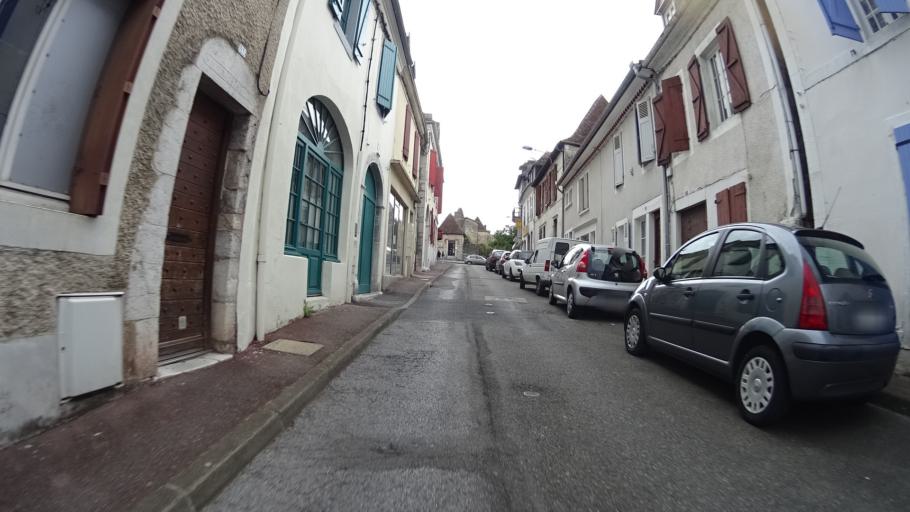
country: FR
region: Aquitaine
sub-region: Departement des Pyrenees-Atlantiques
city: Orthez
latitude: 43.4889
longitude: -0.7766
